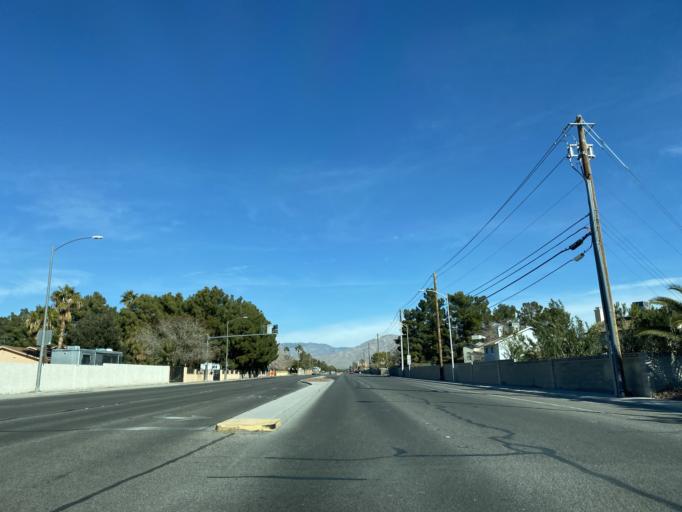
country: US
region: Nevada
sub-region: Clark County
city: Las Vegas
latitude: 36.2538
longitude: -115.2255
